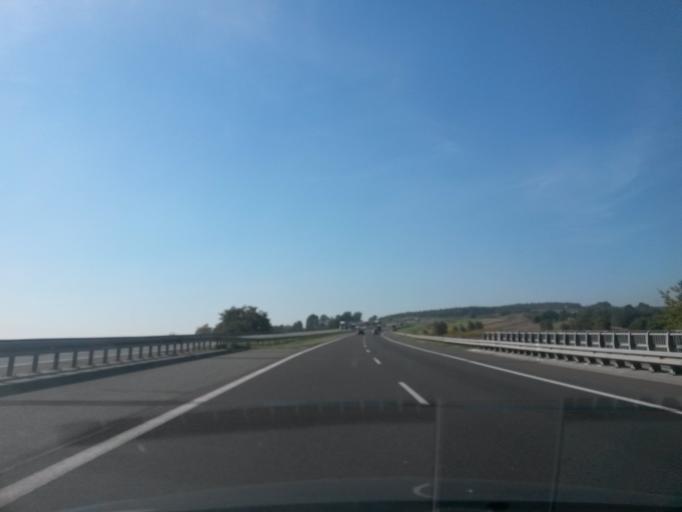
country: PL
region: Lesser Poland Voivodeship
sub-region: Powiat krakowski
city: Mnikow
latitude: 50.0762
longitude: 19.7346
